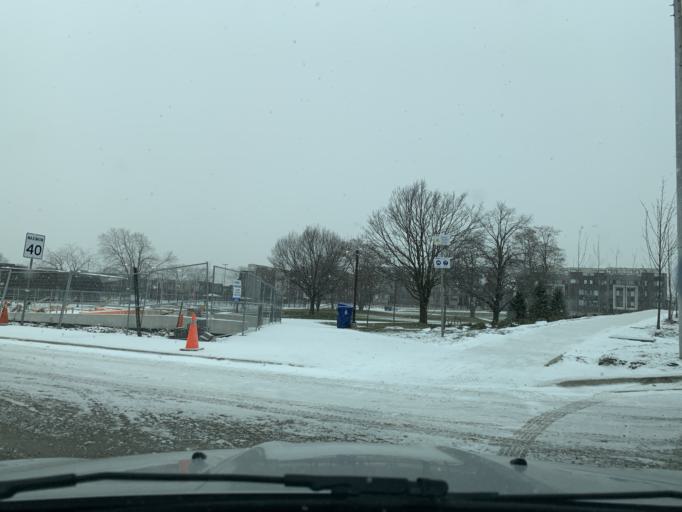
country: CA
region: Ontario
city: Concord
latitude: 43.7339
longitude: -79.4765
